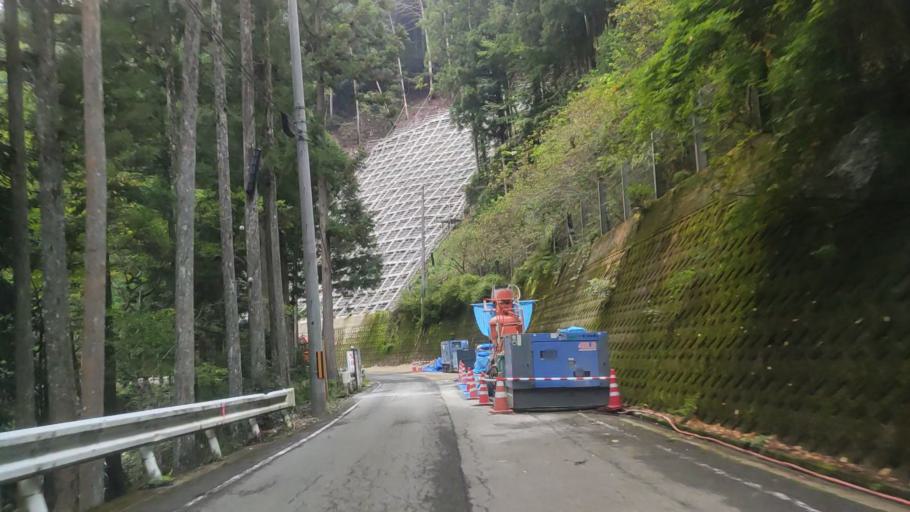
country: JP
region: Wakayama
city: Koya
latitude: 34.2314
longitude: 135.6428
